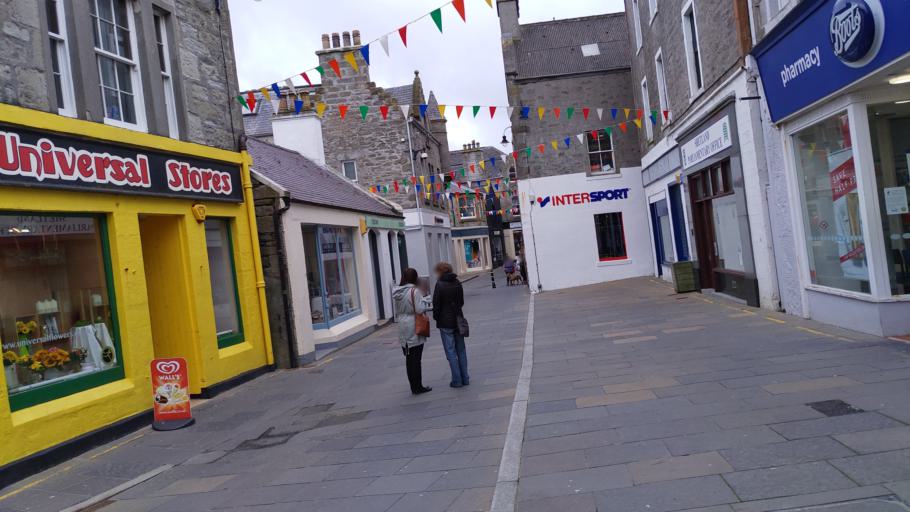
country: GB
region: Scotland
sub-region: Shetland Islands
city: Shetland
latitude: 60.1547
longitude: -1.1440
